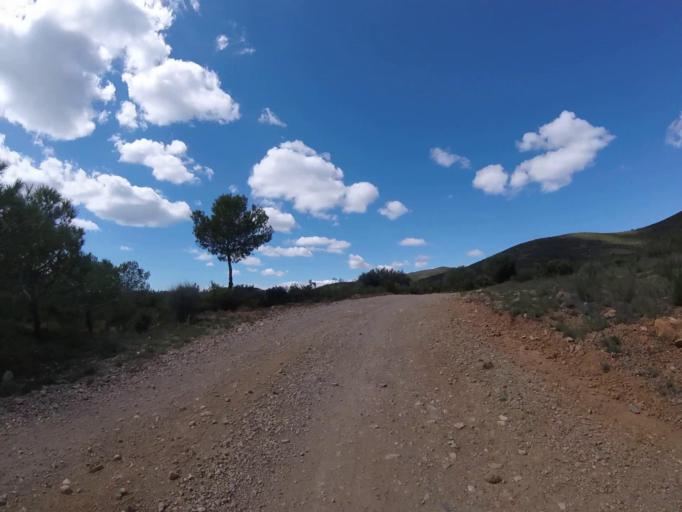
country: ES
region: Valencia
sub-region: Provincia de Castello
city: Santa Magdalena de Pulpis
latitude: 40.3242
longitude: 0.3361
